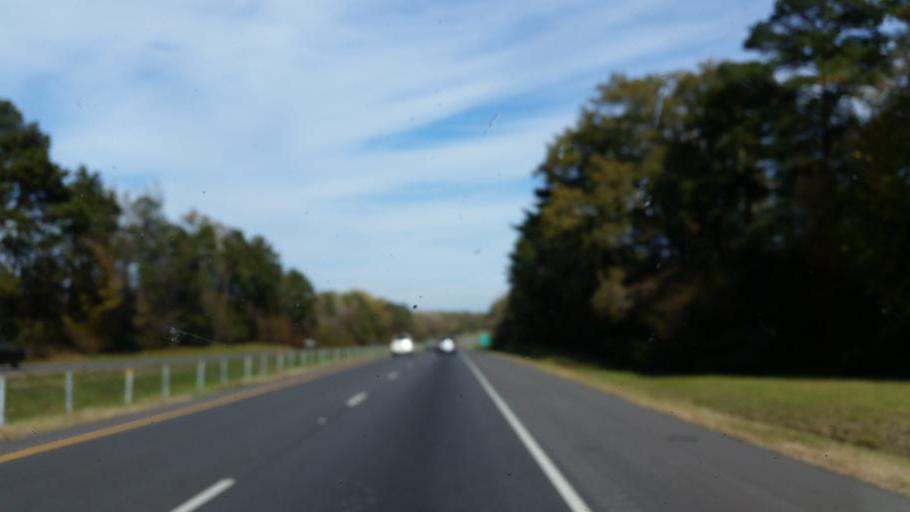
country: US
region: Alabama
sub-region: Greene County
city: Eutaw
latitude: 32.8598
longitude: -87.9365
